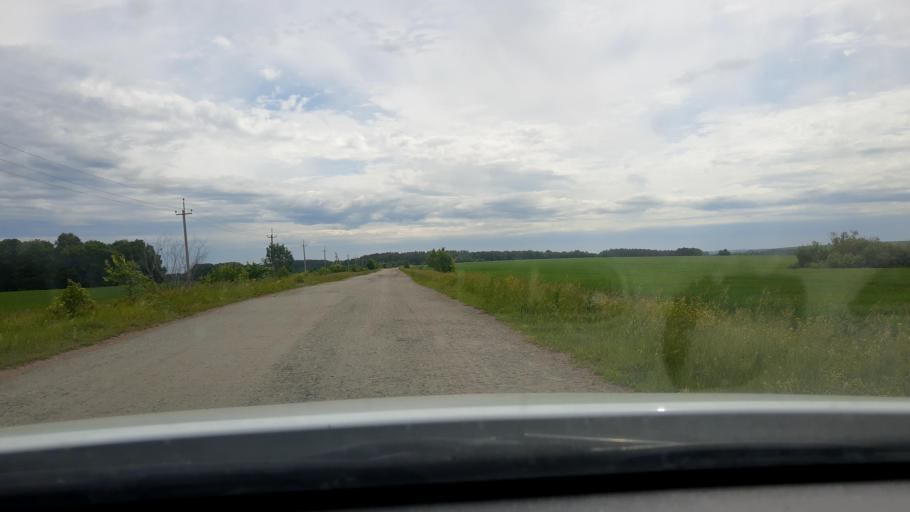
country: RU
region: Bashkortostan
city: Iglino
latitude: 54.7574
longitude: 56.5314
